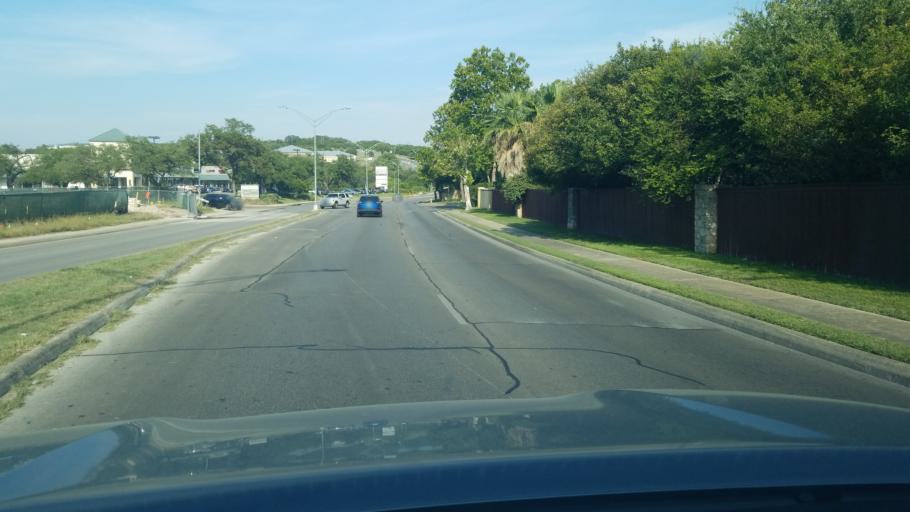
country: US
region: Texas
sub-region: Bexar County
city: Hollywood Park
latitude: 29.6349
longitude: -98.5184
